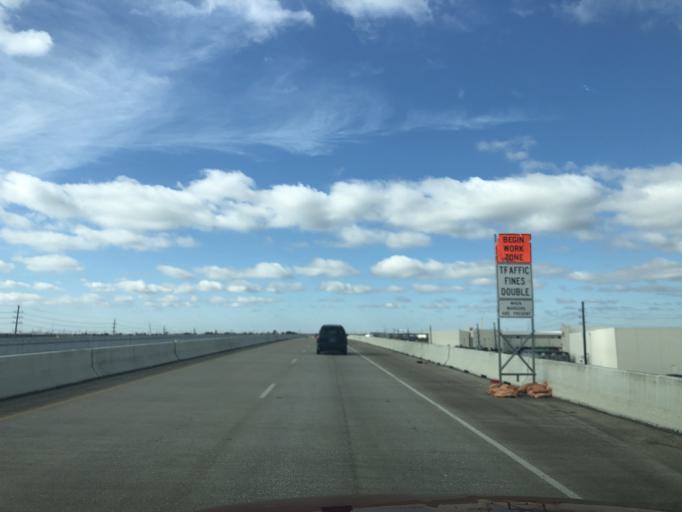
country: US
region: Texas
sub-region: Chambers County
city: Beach City
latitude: 29.7279
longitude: -94.8928
